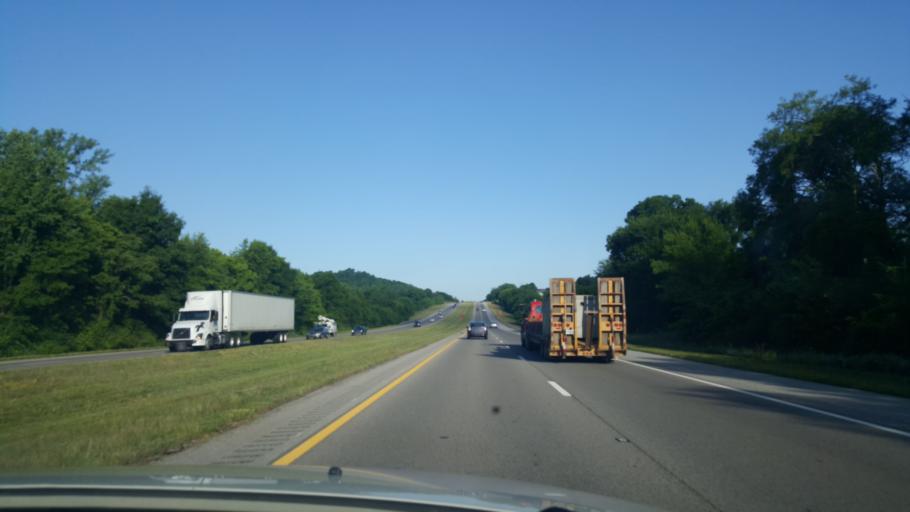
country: US
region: Tennessee
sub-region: Maury County
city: Columbia
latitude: 35.6275
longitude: -87.0837
